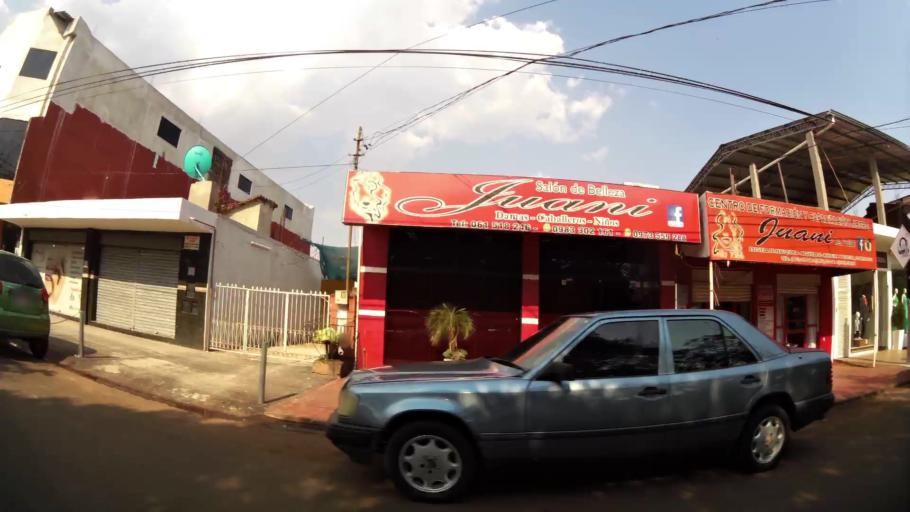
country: PY
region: Alto Parana
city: Presidente Franco
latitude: -25.5342
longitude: -54.6238
